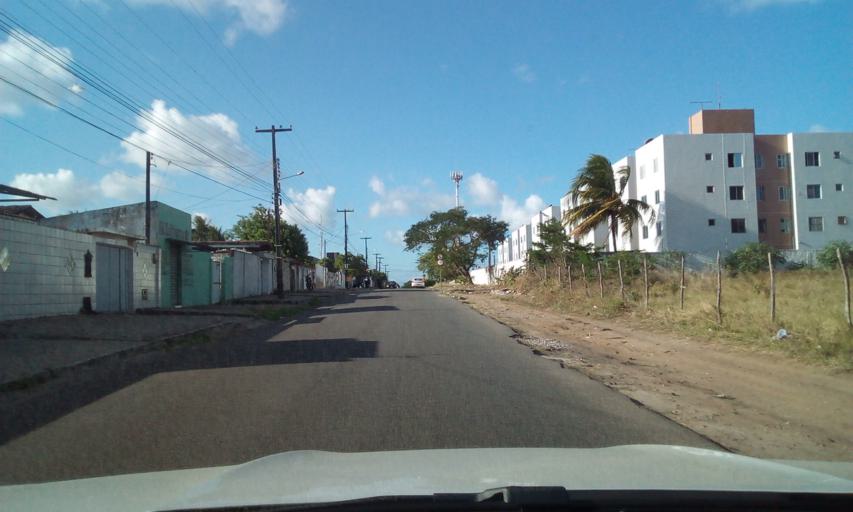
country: BR
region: Paraiba
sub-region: Bayeux
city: Bayeux
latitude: -7.1408
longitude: -34.9111
